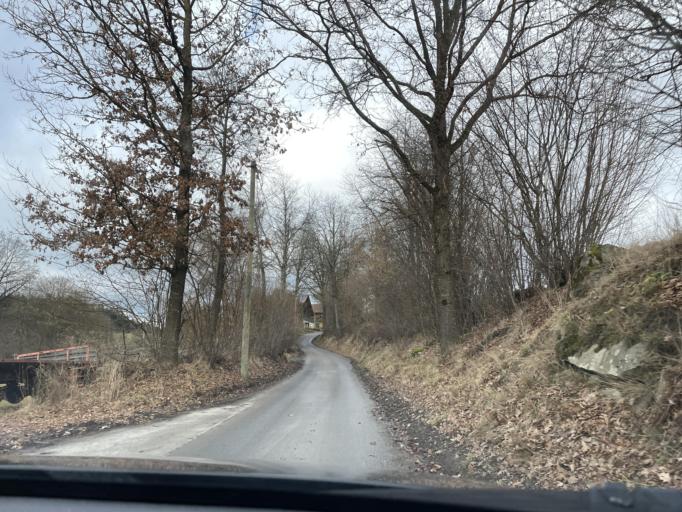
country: DE
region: Bavaria
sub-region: Upper Palatinate
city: Blaibach
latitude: 49.1364
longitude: 12.8328
